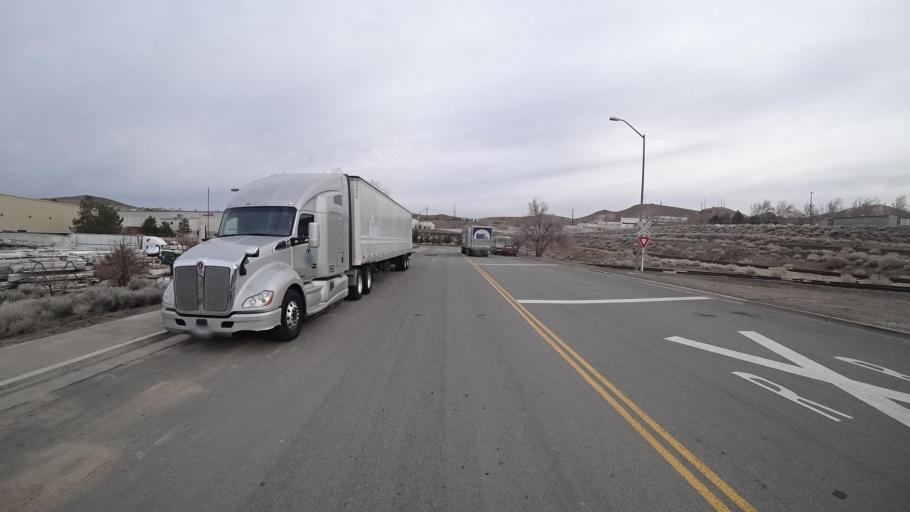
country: US
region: Nevada
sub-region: Washoe County
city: Reno
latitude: 39.5710
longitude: -119.8126
